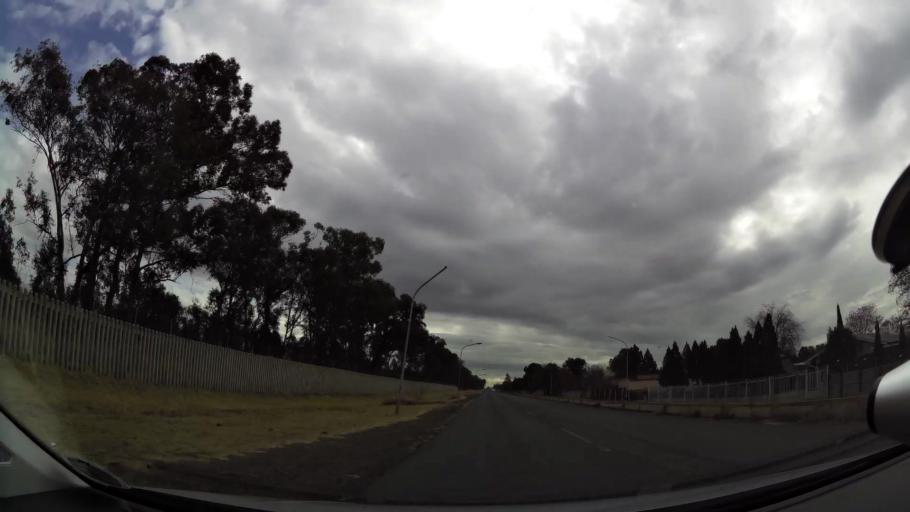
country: ZA
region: Orange Free State
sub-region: Fezile Dabi District Municipality
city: Kroonstad
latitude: -27.6384
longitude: 27.2196
